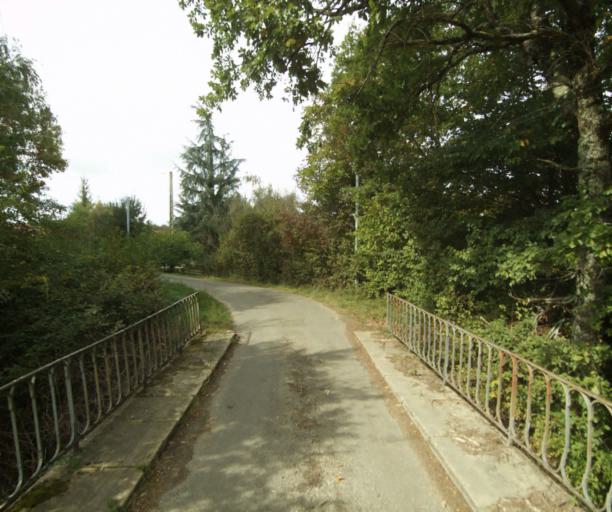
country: FR
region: Midi-Pyrenees
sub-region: Departement du Gers
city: Eauze
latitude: 43.8364
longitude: 0.0989
